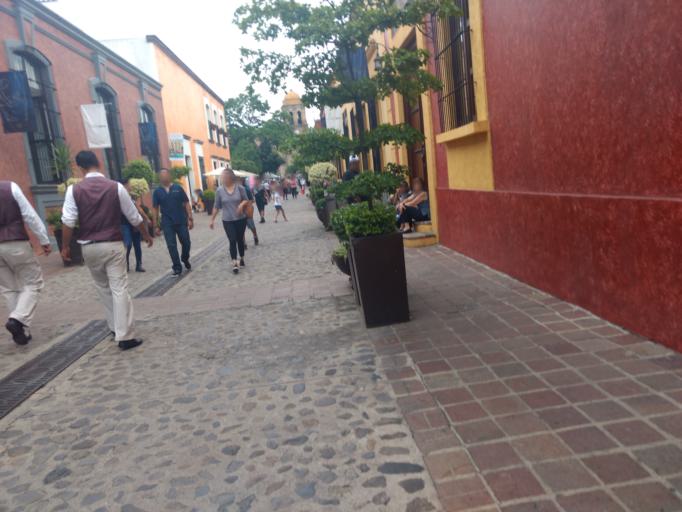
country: MX
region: Jalisco
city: Tequila
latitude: 20.8854
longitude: -103.8402
